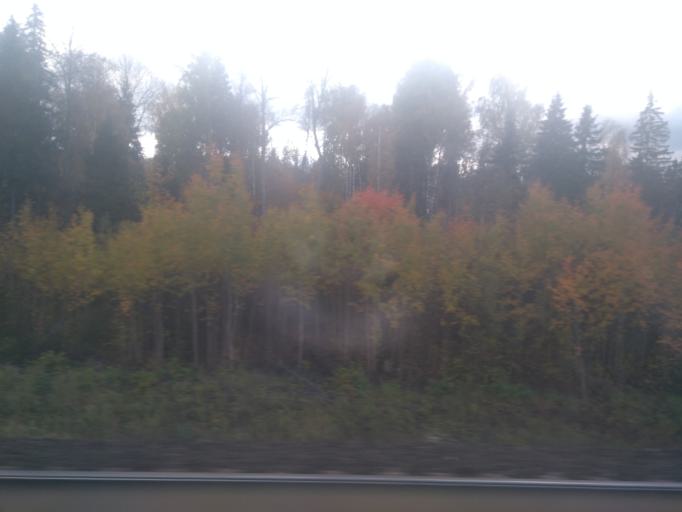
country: RU
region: Udmurtiya
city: Mozhga
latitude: 56.4266
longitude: 52.0433
